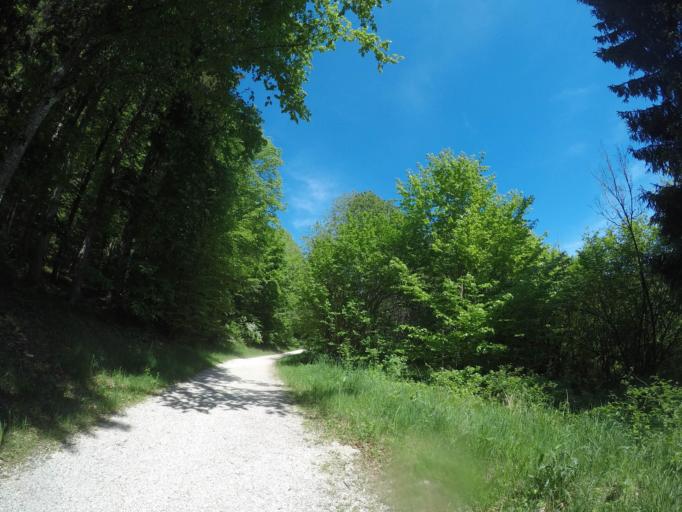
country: DE
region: Baden-Wuerttemberg
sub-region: Tuebingen Region
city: Blaubeuren
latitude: 48.3957
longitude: 9.7655
